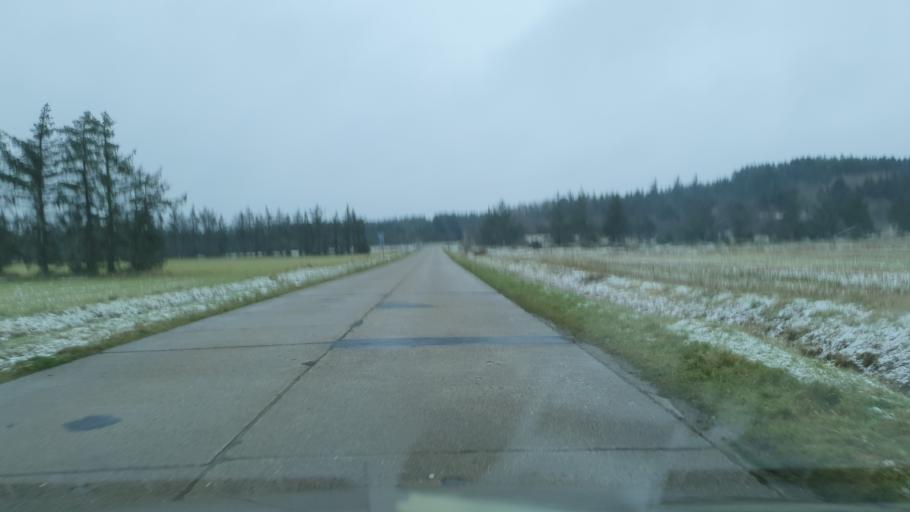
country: DK
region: North Denmark
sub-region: Jammerbugt Kommune
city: Brovst
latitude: 57.1448
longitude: 9.4546
